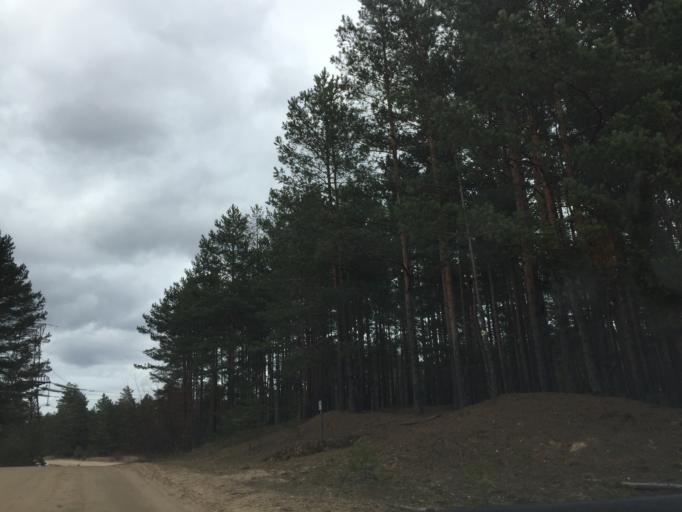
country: LV
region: Daugavpils
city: Daugavpils
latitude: 55.9089
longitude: 26.5393
